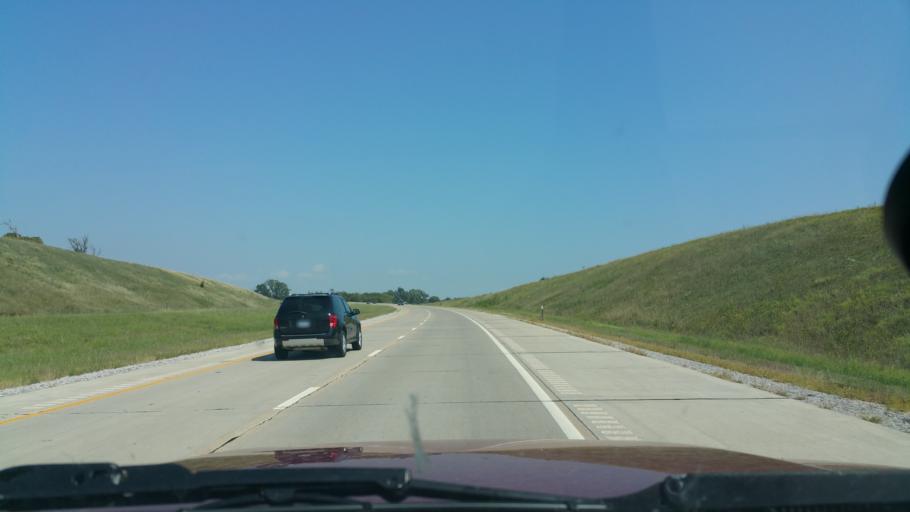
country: US
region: Kansas
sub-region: Dickinson County
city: Abilene
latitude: 38.9438
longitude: -97.1527
